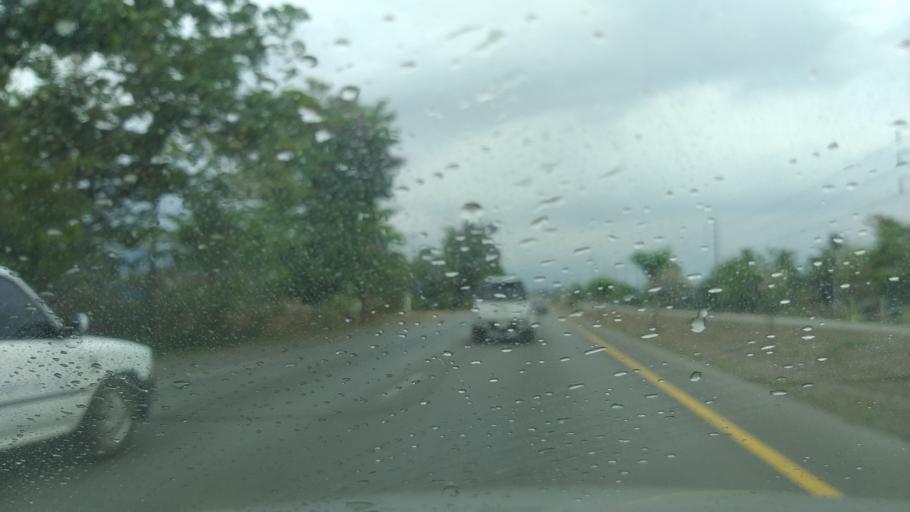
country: TH
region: Chanthaburi
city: Khlung
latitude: 12.4240
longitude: 102.3205
